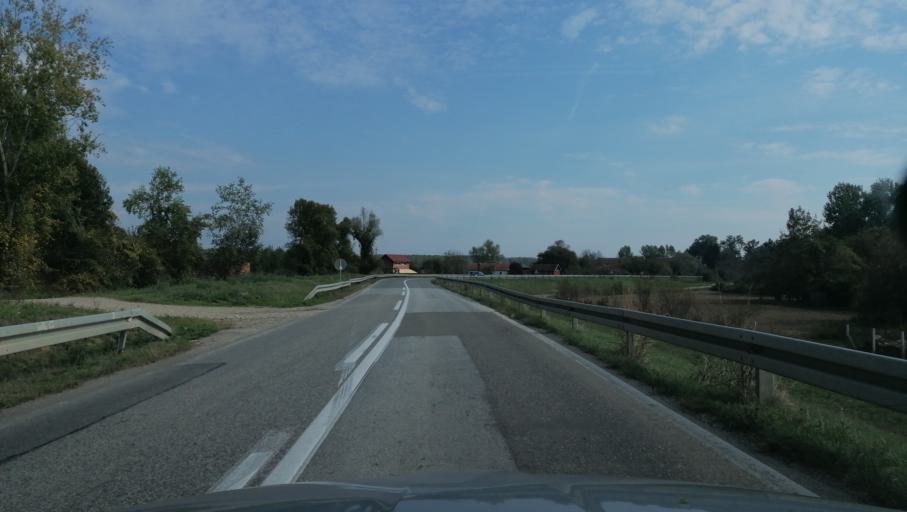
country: BA
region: Republika Srpska
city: Balatun
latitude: 44.8945
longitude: 19.3303
